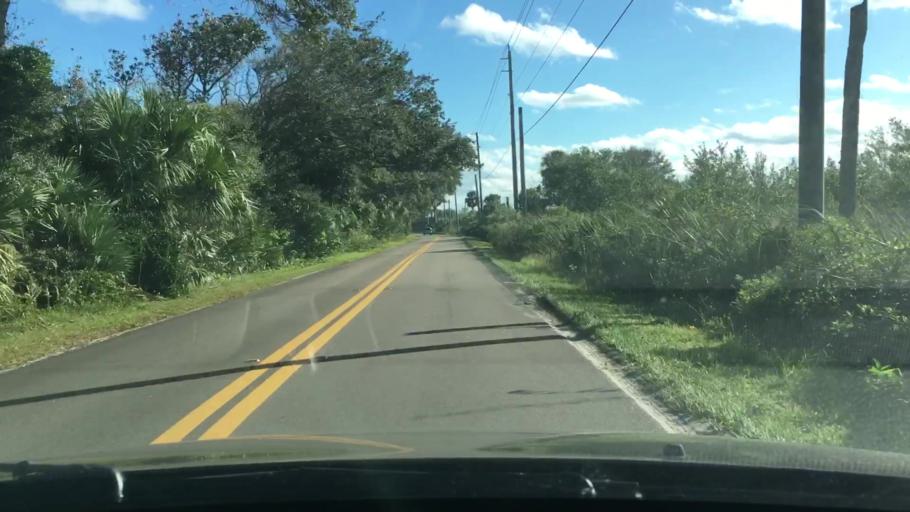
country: US
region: Florida
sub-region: Volusia County
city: Ormond-by-the-Sea
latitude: 29.4039
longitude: -81.0958
